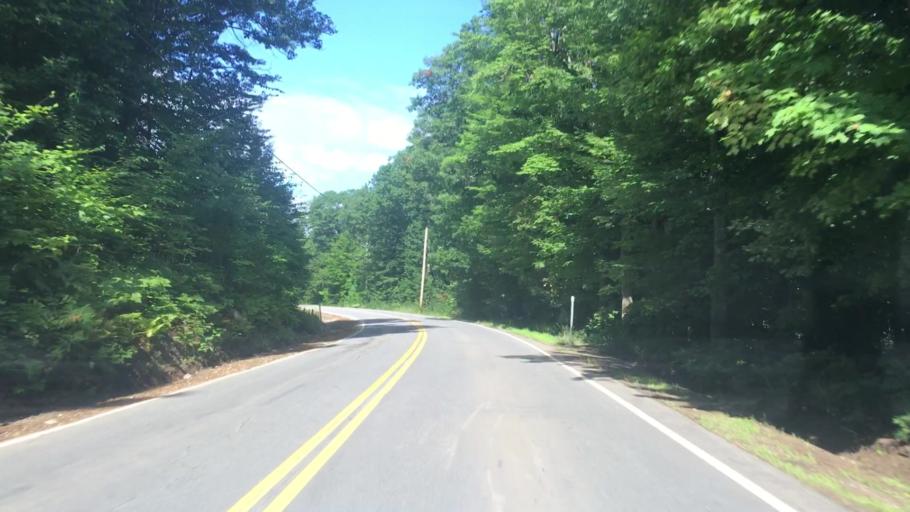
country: US
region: New Hampshire
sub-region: Belknap County
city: Gilford
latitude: 43.5393
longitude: -71.3164
